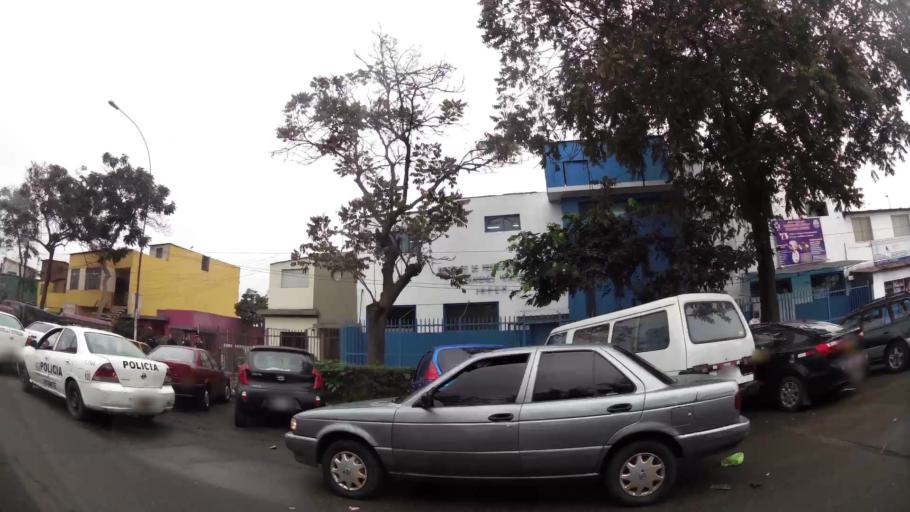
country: PE
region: Lima
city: Lima
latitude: -12.0627
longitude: -77.0253
